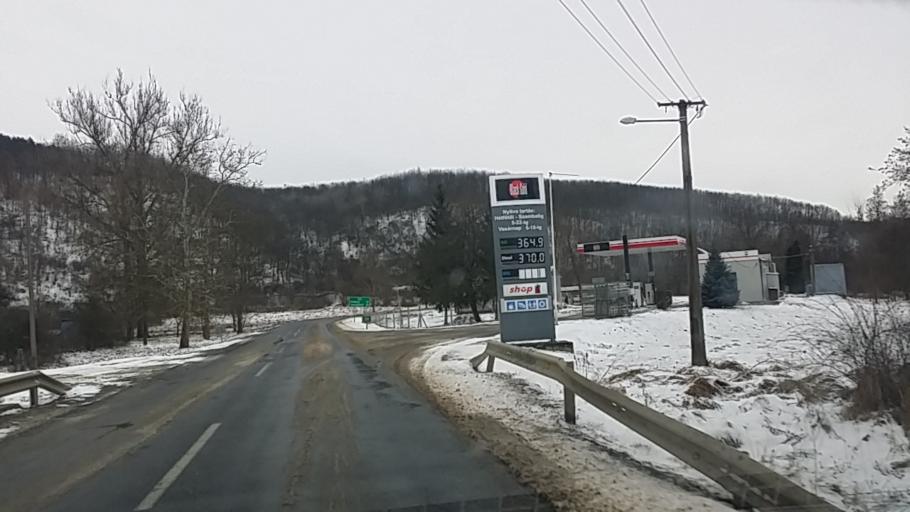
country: HU
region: Borsod-Abauj-Zemplen
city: Szendro
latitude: 48.3975
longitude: 20.7390
